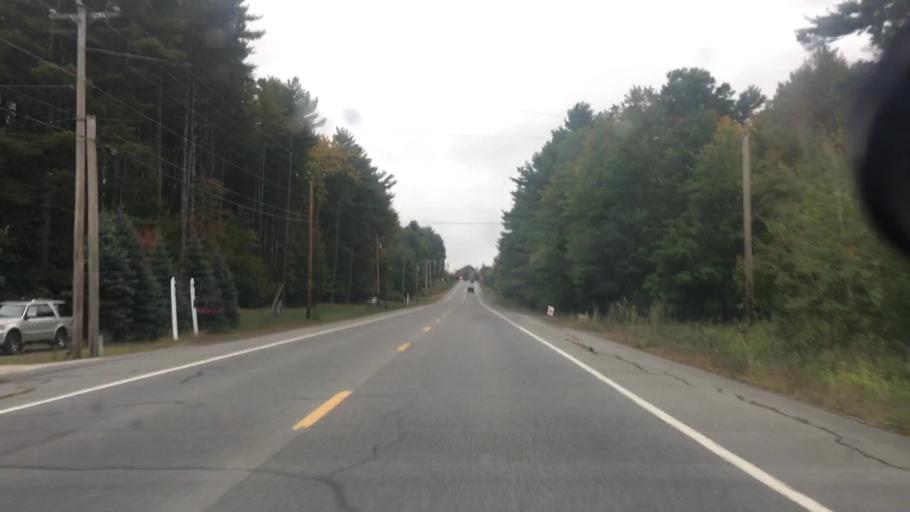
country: US
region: Maine
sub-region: Kennebec County
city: Belgrade
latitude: 44.4018
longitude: -69.8101
